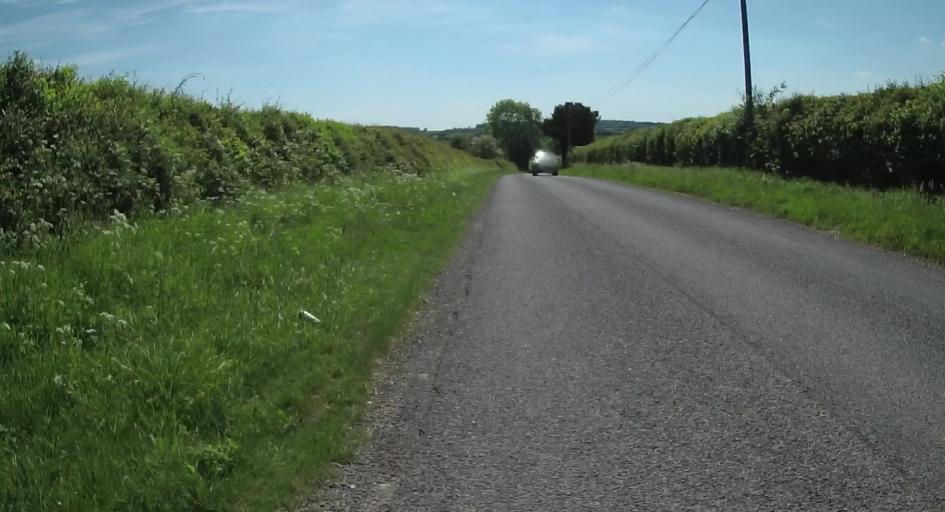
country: GB
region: England
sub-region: Hampshire
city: Four Marks
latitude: 51.1582
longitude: -1.1358
